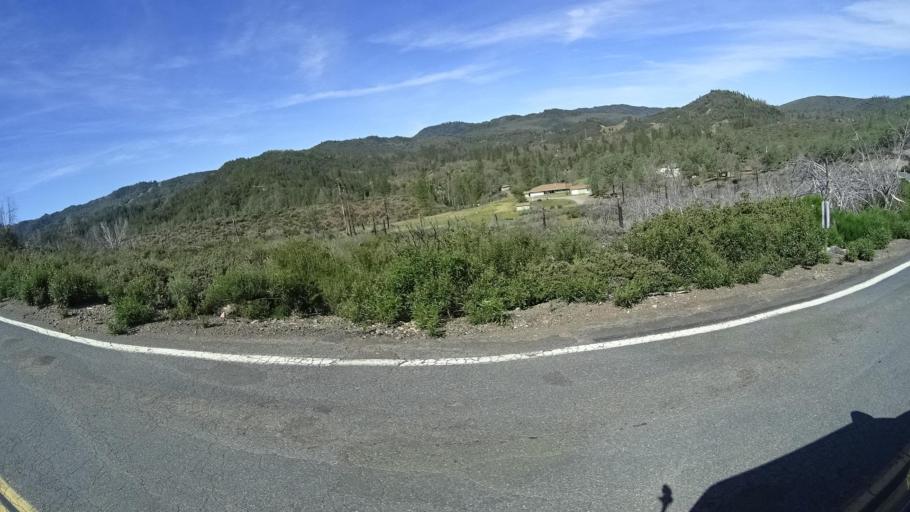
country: US
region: California
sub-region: Lake County
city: Cobb
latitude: 38.8565
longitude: -122.7539
